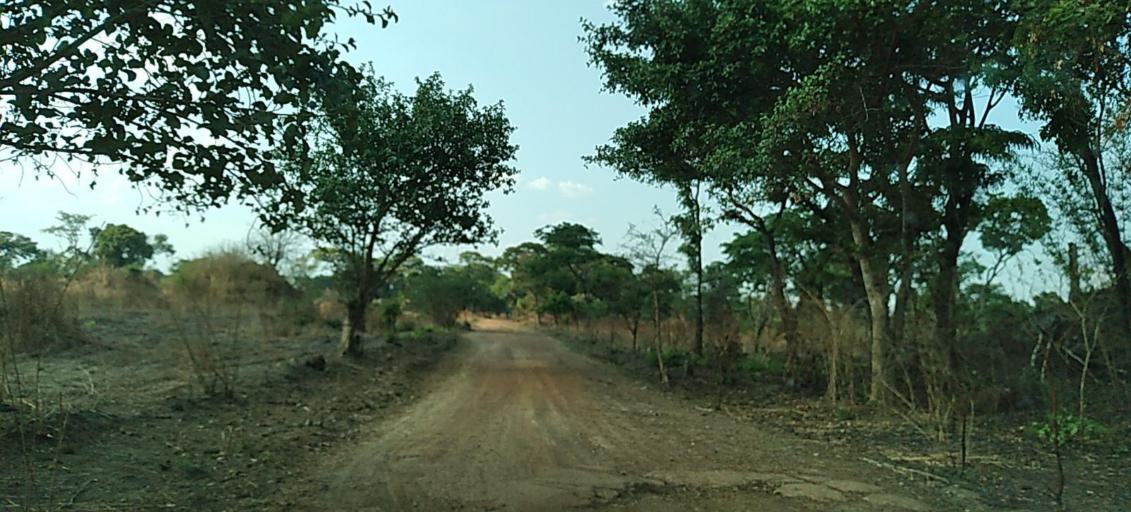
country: ZM
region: Copperbelt
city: Mpongwe
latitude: -13.4606
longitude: 28.0684
